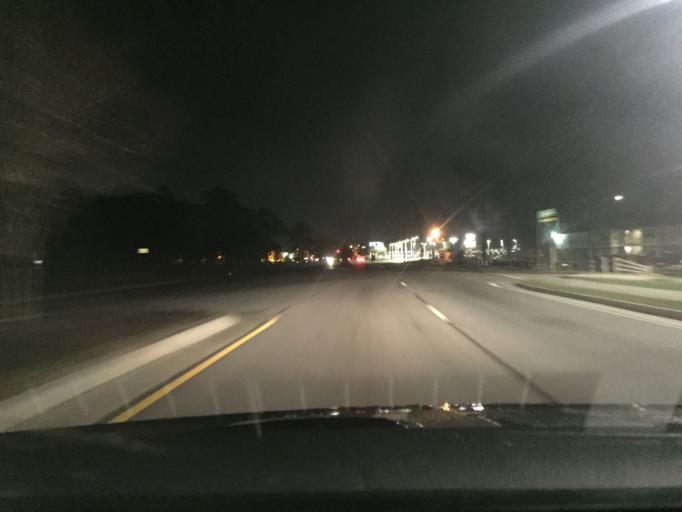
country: US
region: Georgia
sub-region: Chatham County
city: Montgomery
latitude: 32.0004
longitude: -81.1312
